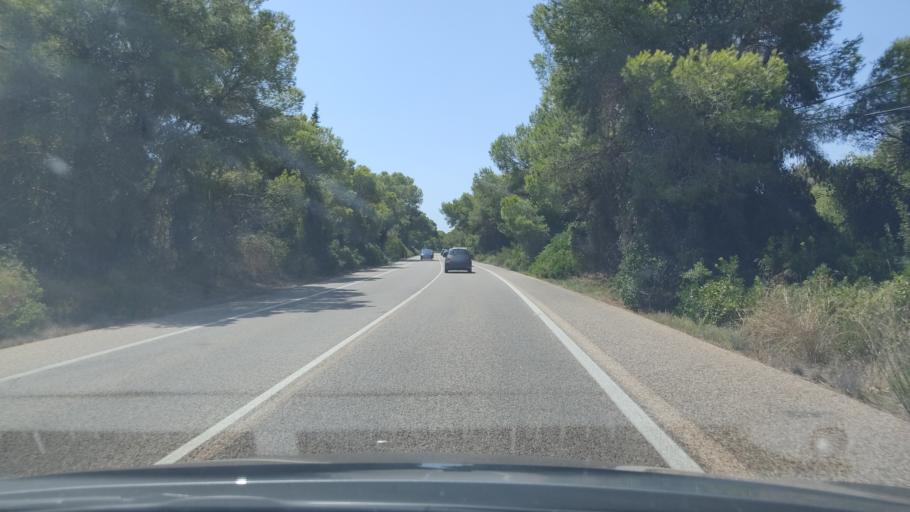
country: ES
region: Valencia
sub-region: Provincia de Valencia
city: Sollana
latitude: 39.3285
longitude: -0.3117
